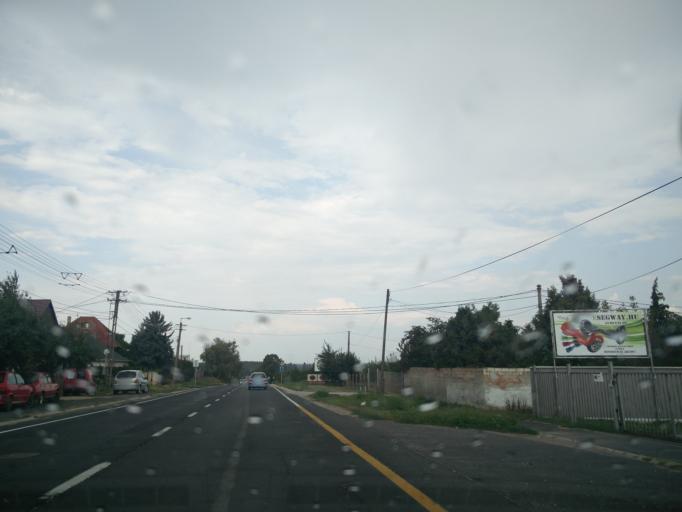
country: HU
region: Fejer
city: Szabadbattyan
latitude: 47.0979
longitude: 18.3498
